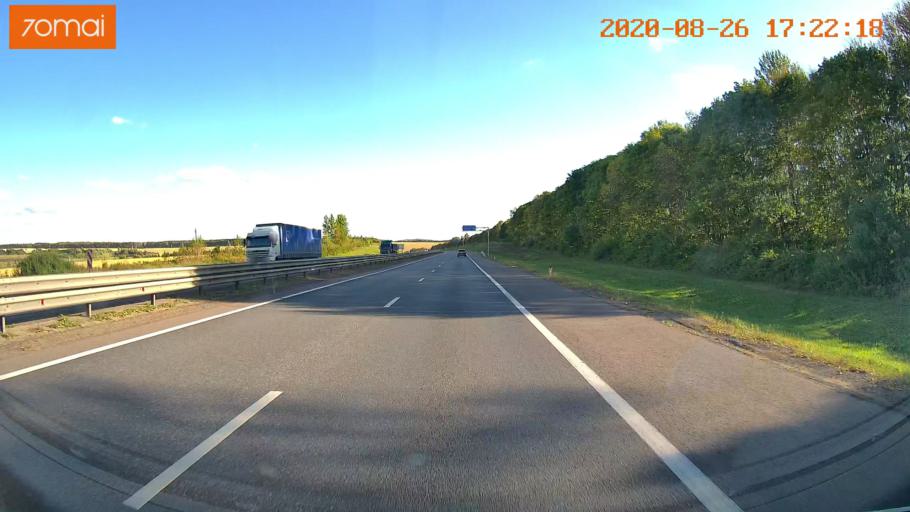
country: RU
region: Tula
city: Volovo
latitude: 53.5519
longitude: 38.1125
